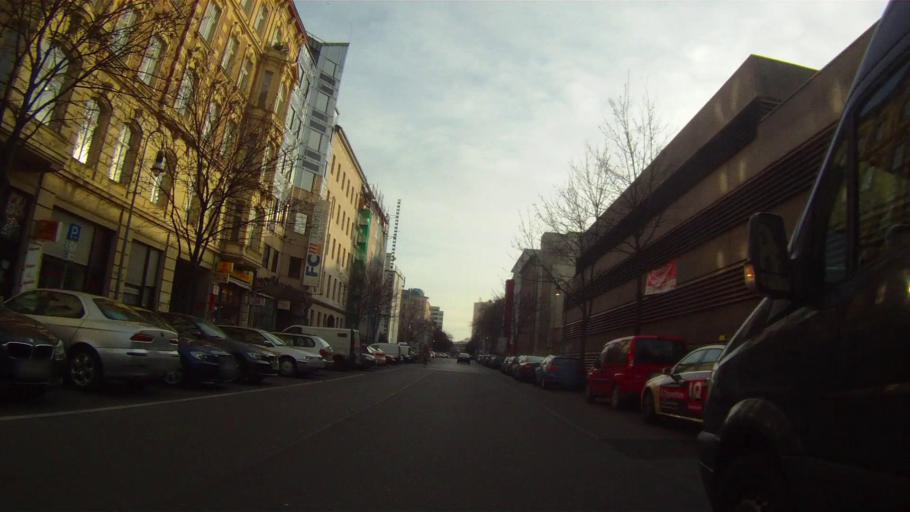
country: DE
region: Berlin
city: Bezirk Kreuzberg
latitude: 52.5009
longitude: 13.4121
